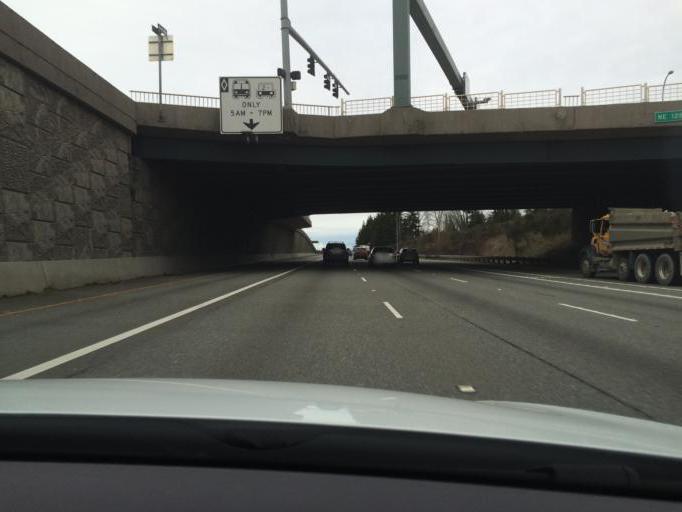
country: US
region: Washington
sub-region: King County
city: Kingsgate
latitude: 47.7141
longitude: -122.1847
